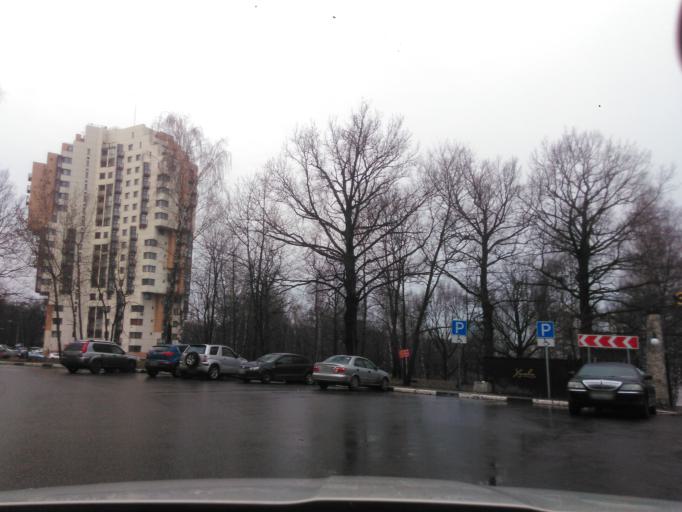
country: RU
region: Moskovskaya
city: Levoberezhnaya
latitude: 55.8921
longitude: 37.4699
